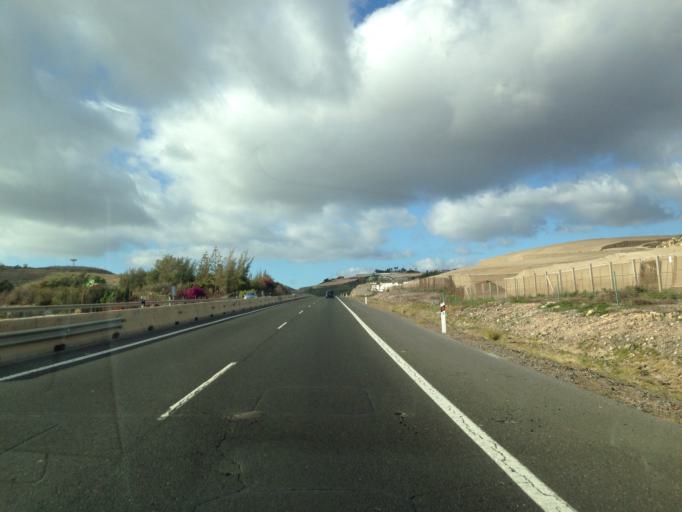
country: ES
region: Canary Islands
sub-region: Provincia de Las Palmas
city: Maspalomas
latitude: 27.7587
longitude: -15.6218
